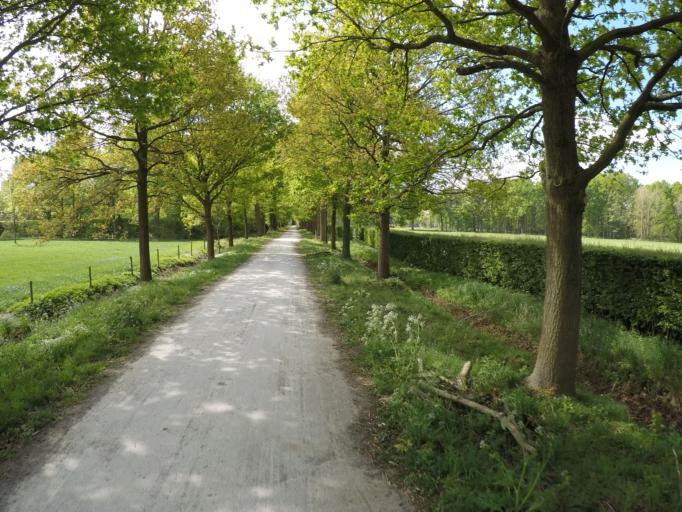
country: BE
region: Flanders
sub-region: Provincie Antwerpen
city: Berlaar
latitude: 51.1252
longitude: 4.6836
